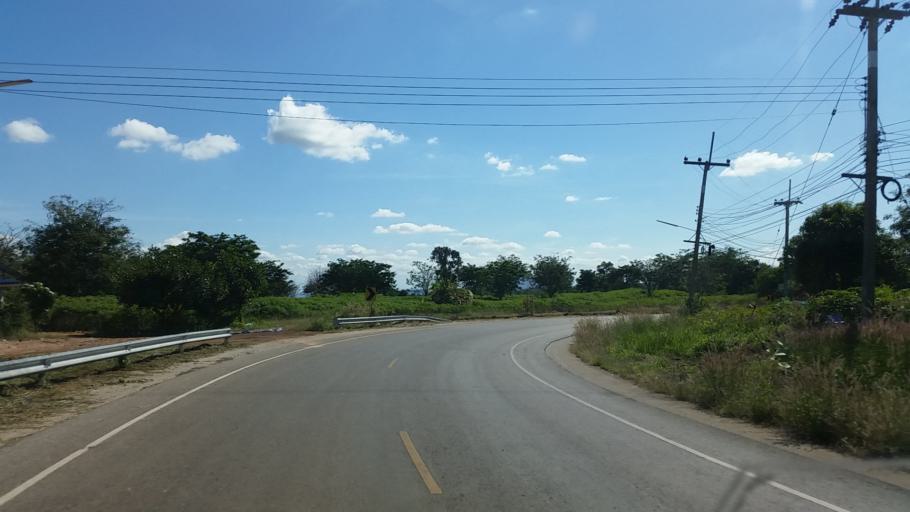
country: TH
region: Chaiyaphum
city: Thep Sathit
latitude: 15.5672
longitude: 101.4163
